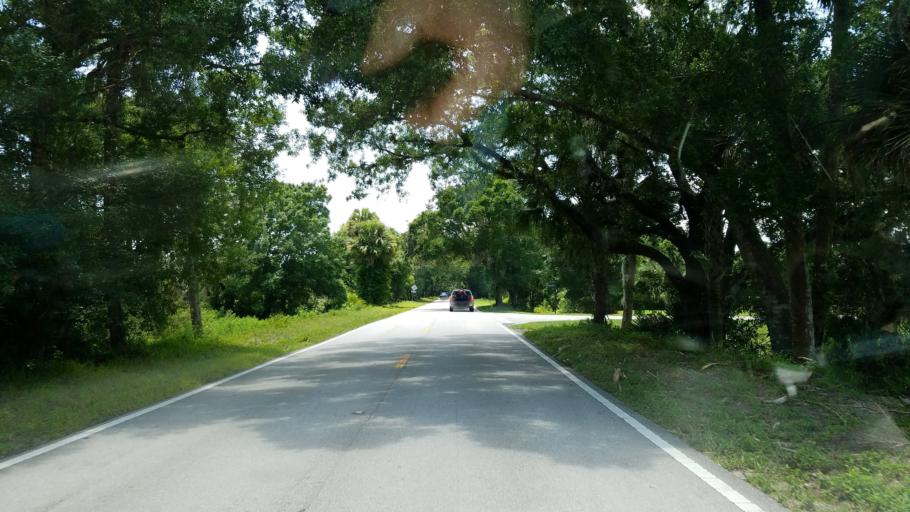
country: US
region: Florida
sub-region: Martin County
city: Indiantown
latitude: 27.1622
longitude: -80.5986
